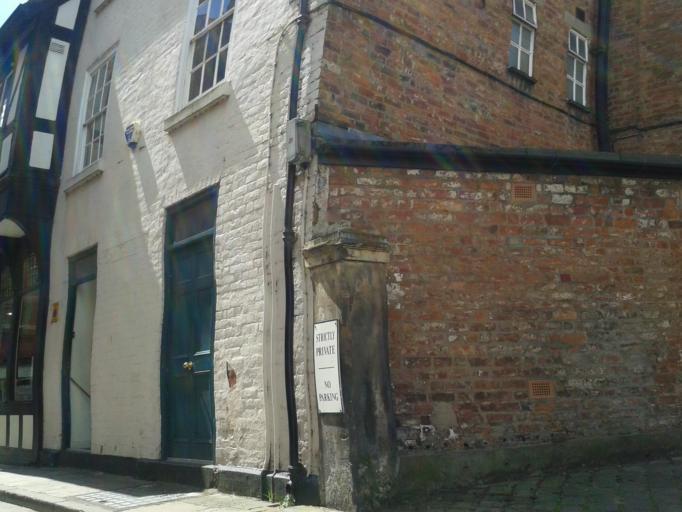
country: GB
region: England
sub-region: Shropshire
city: Shrewsbury
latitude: 52.7101
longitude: -2.7513
